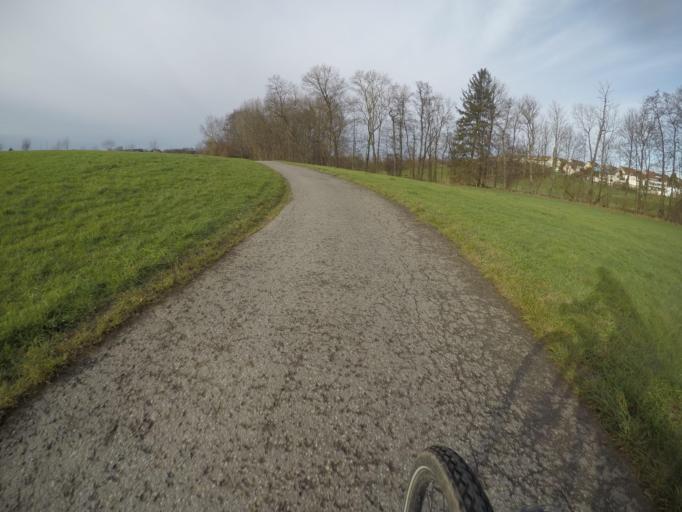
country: DE
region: Baden-Wuerttemberg
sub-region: Regierungsbezirk Stuttgart
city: Leutenbach
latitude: 48.8953
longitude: 9.3742
